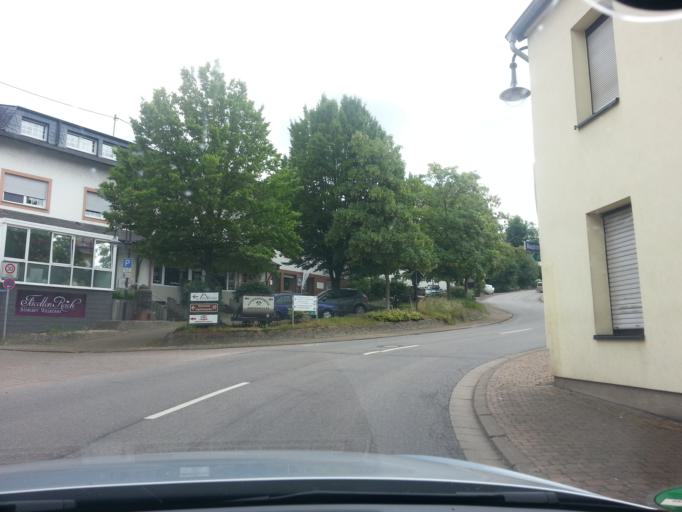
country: DE
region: Saarland
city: Nalbach
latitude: 49.4143
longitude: 6.7665
